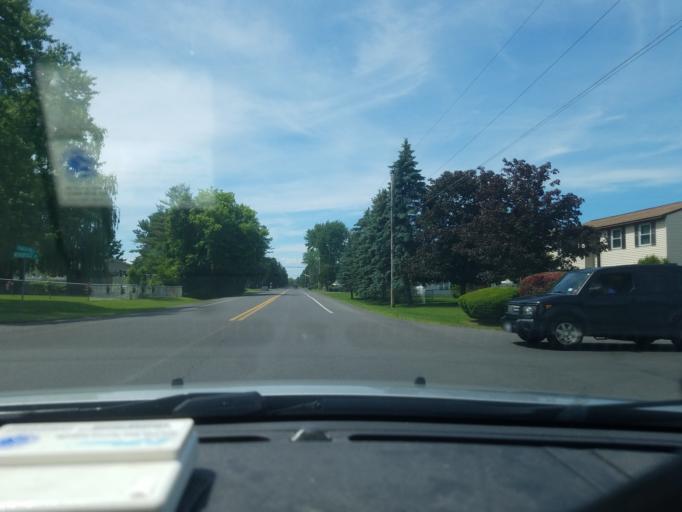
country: US
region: New York
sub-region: Onondaga County
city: East Syracuse
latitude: 43.0792
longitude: -76.0693
